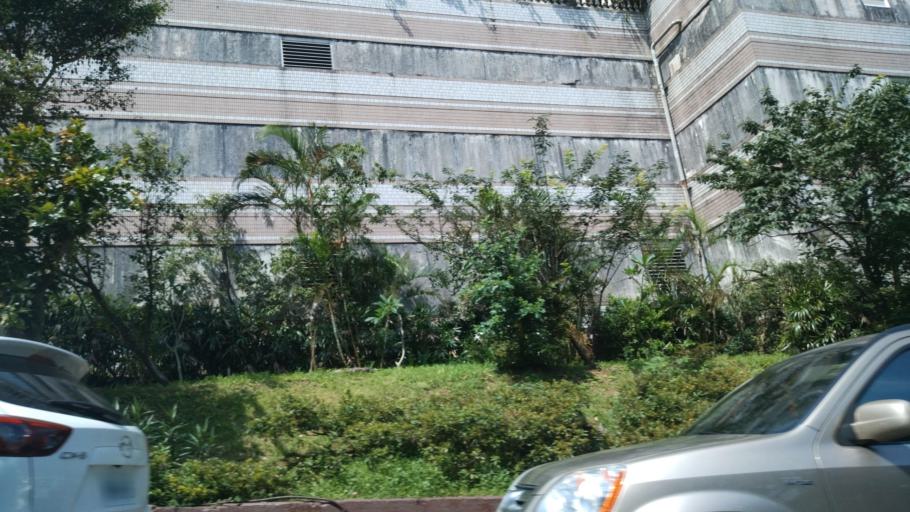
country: TW
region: Taipei
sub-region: Taipei
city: Banqiao
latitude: 24.9395
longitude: 121.5027
